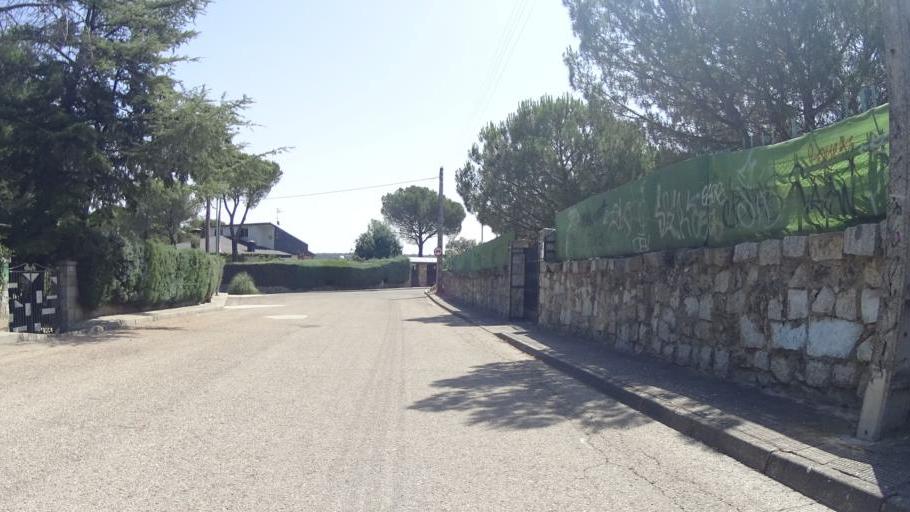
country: ES
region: Madrid
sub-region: Provincia de Madrid
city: Colmenarejo
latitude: 40.5585
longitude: -4.0073
